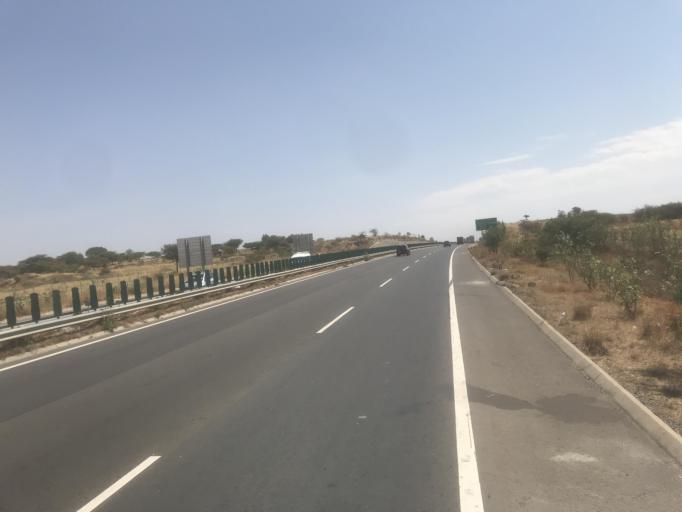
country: ET
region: Oromiya
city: Mojo
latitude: 8.5846
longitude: 39.1654
